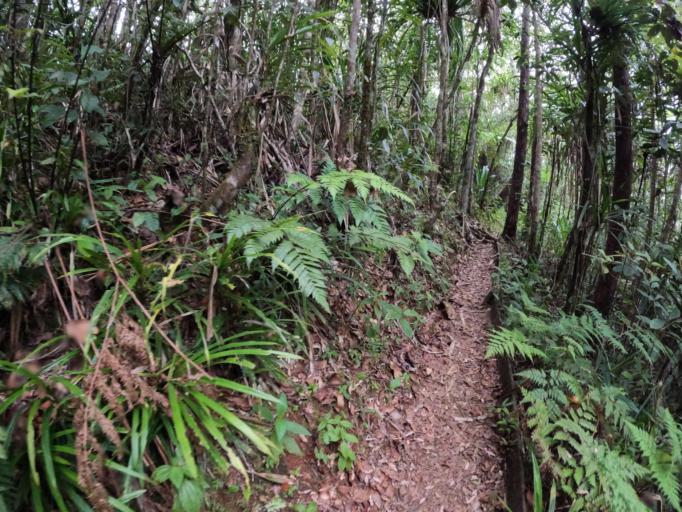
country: FJ
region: Central
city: Suva
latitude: -18.0565
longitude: 178.4629
